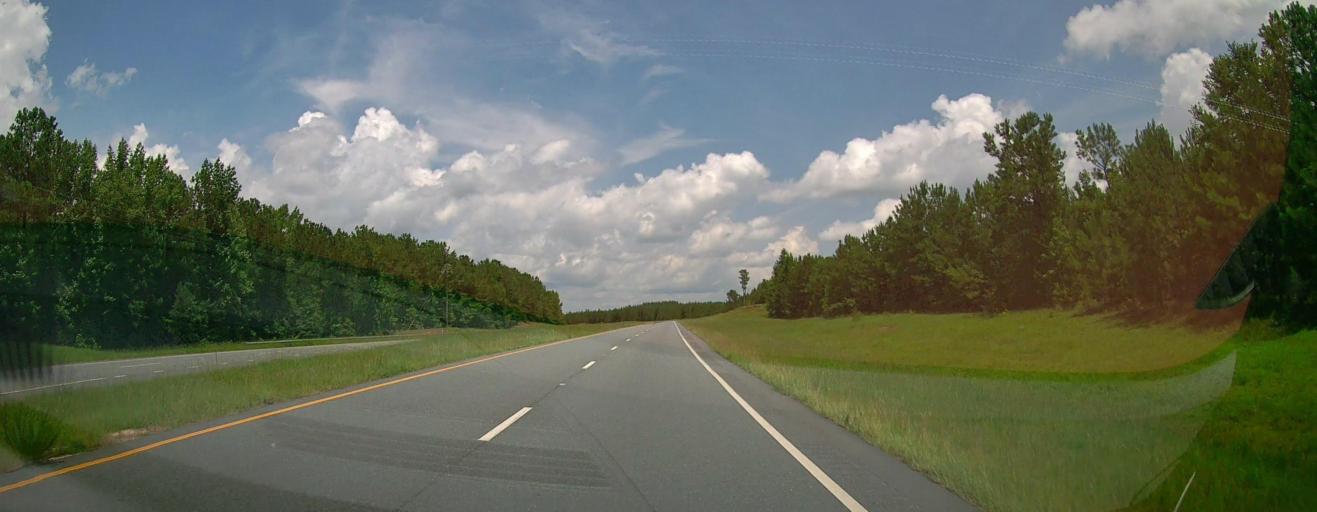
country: US
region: Georgia
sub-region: Upson County
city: Thomaston
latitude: 32.7749
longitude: -84.2478
